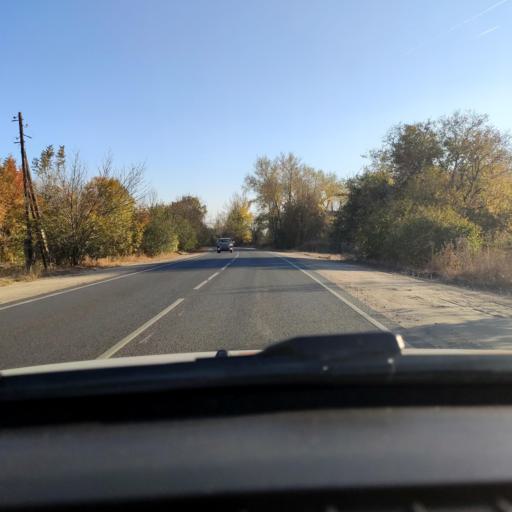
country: RU
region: Voronezj
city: Shilovo
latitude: 51.5700
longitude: 39.1386
